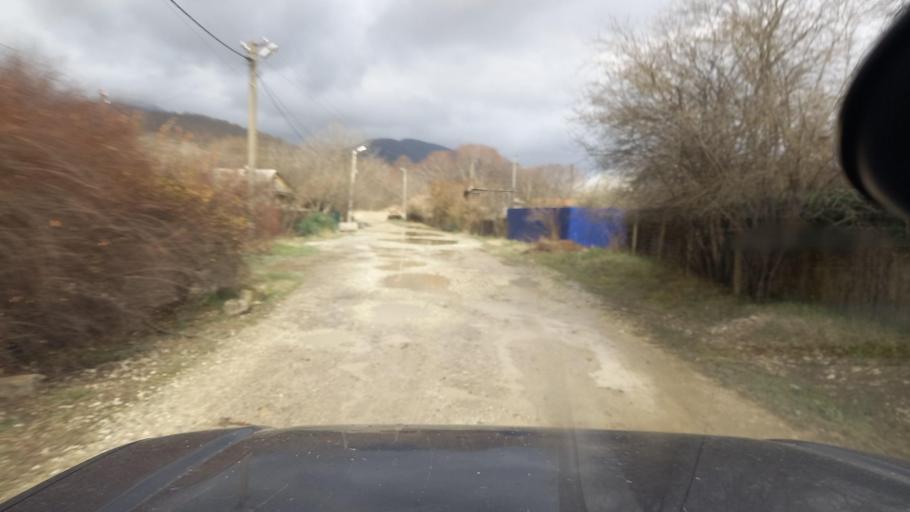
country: RU
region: Krasnodarskiy
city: Pshada
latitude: 44.4800
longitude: 38.4020
